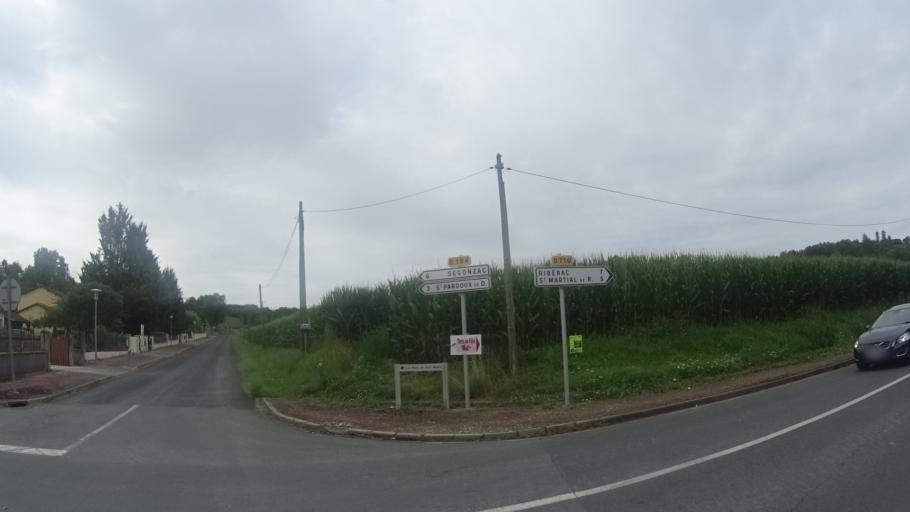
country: FR
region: Aquitaine
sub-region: Departement de la Dordogne
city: Tocane-Saint-Apre
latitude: 45.2483
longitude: 0.4182
